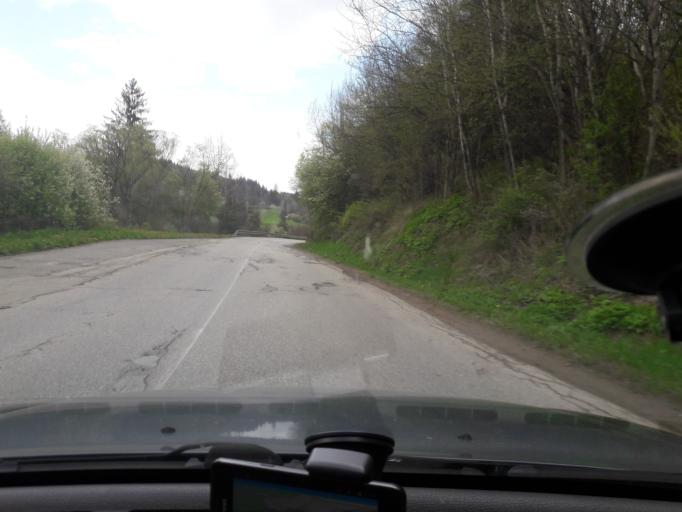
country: SK
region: Banskobystricky
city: Cierny Balog
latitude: 48.7600
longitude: 19.6282
